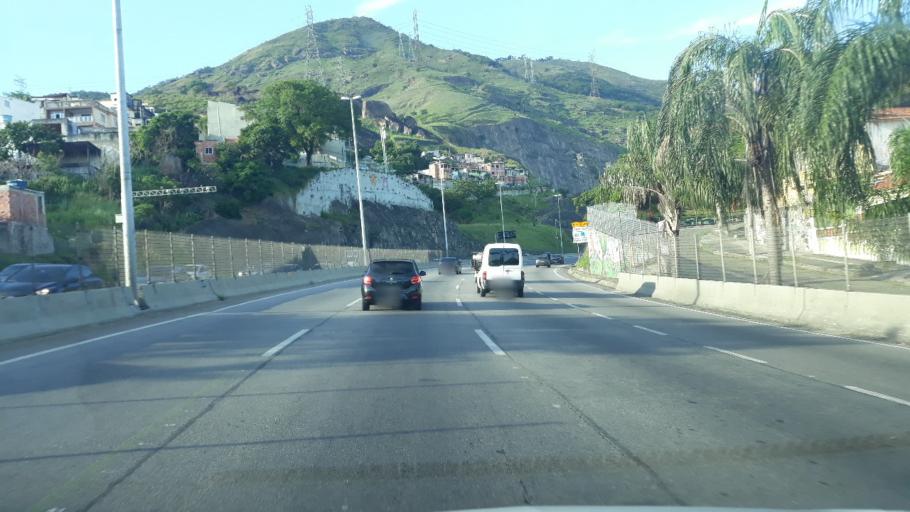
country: BR
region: Rio de Janeiro
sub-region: Rio De Janeiro
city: Rio de Janeiro
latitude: -22.9053
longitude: -43.3050
